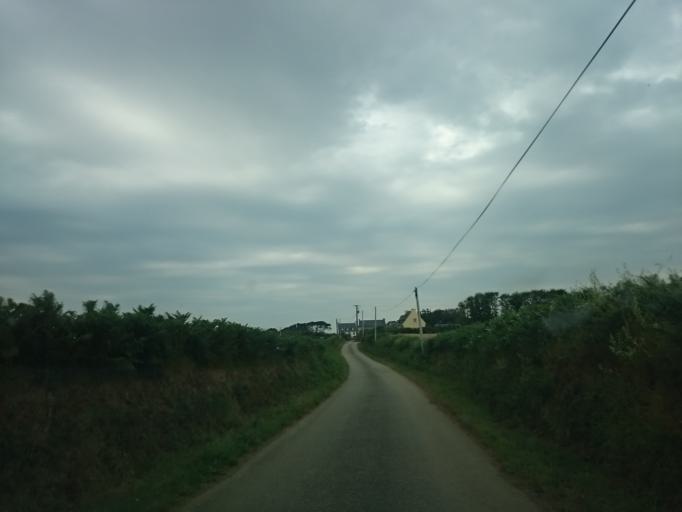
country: FR
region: Brittany
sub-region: Departement du Finistere
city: Le Conquet
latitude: 48.4008
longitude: -4.7666
